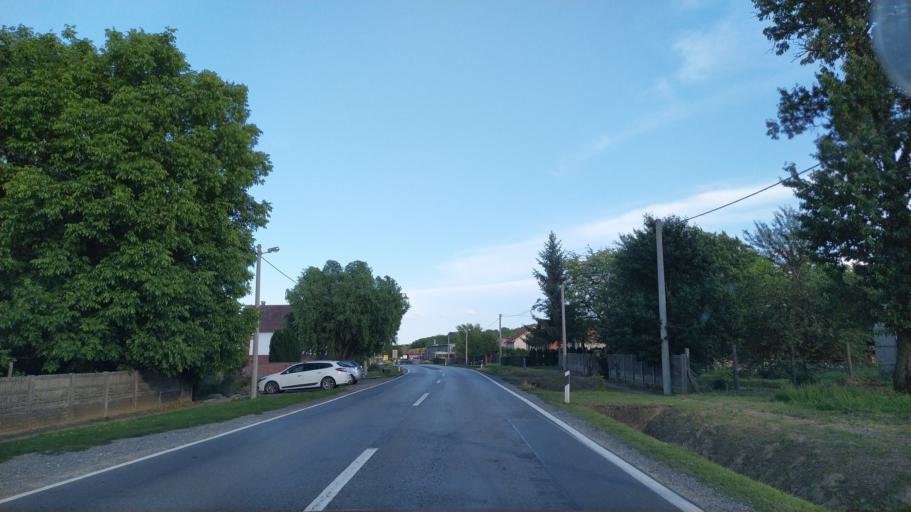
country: HR
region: Virovitick-Podravska
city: Slatina
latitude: 45.7279
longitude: 17.6313
